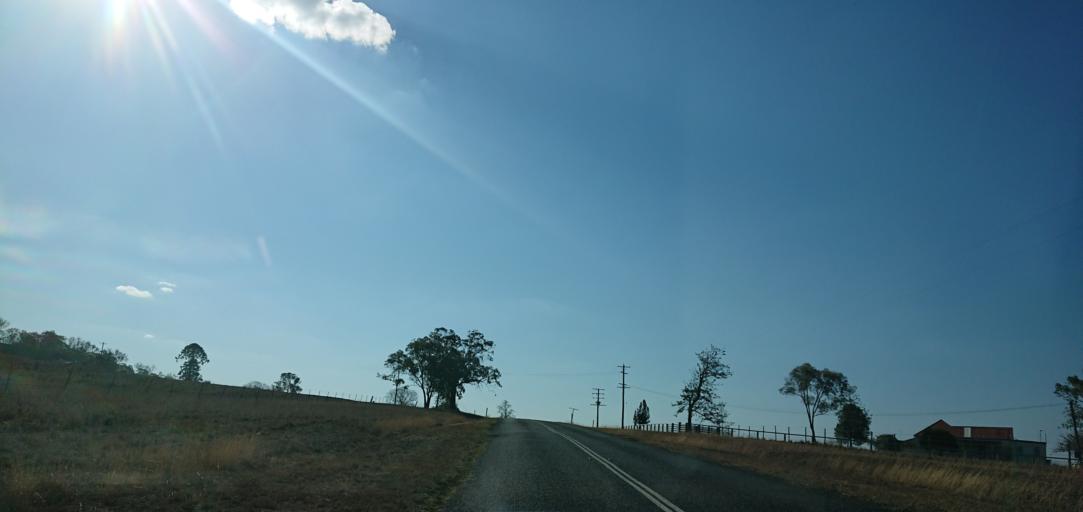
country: AU
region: Queensland
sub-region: Toowoomba
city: Westbrook
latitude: -27.7007
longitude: 151.7166
